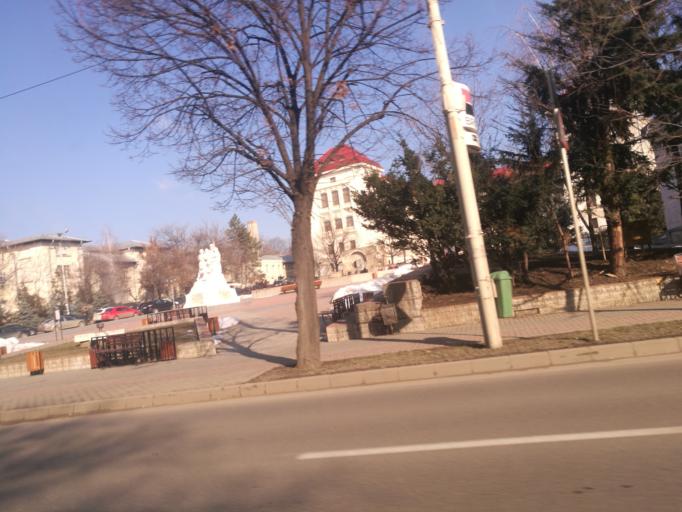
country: RO
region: Iasi
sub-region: Municipiul Iasi
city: Iasi
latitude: 47.1673
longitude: 27.5841
